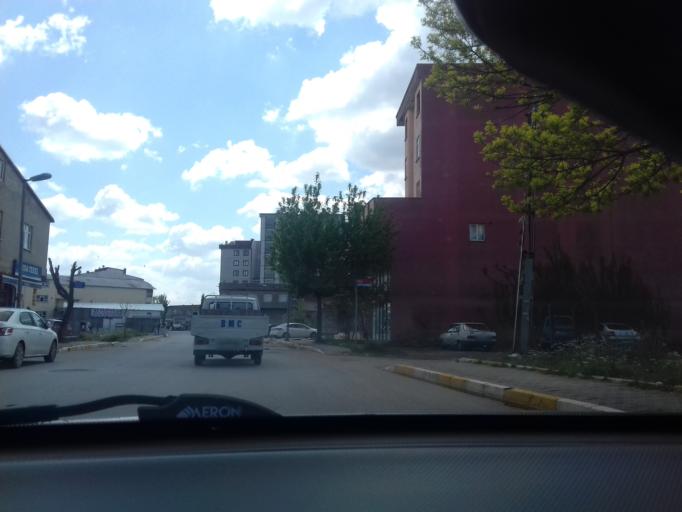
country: TR
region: Istanbul
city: Pendik
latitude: 40.8913
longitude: 29.2779
